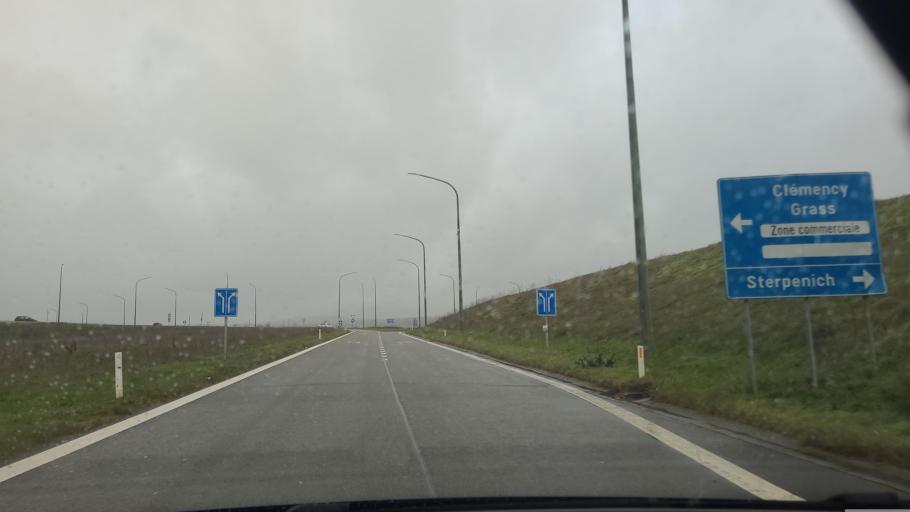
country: LU
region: Luxembourg
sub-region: Canton de Capellen
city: Steinfort
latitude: 49.6404
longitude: 5.8900
